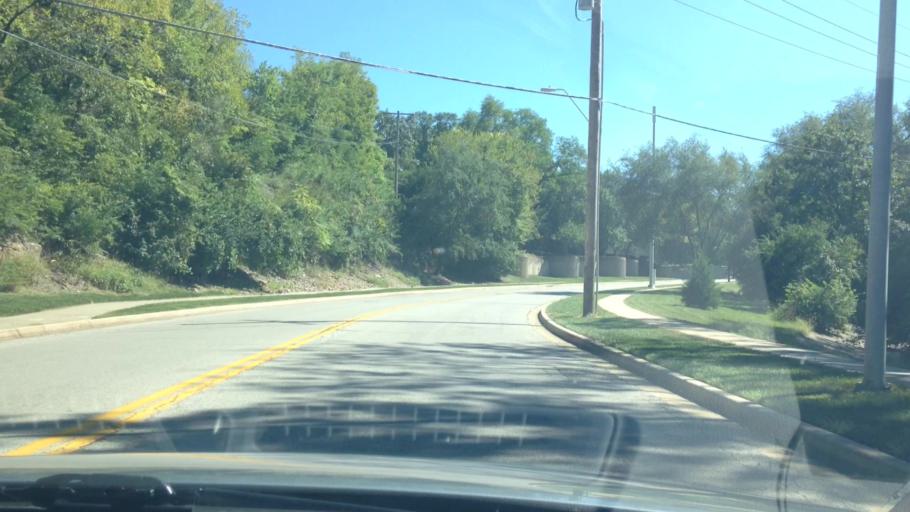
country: US
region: Missouri
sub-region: Jackson County
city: Raytown
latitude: 39.0113
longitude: -94.5051
